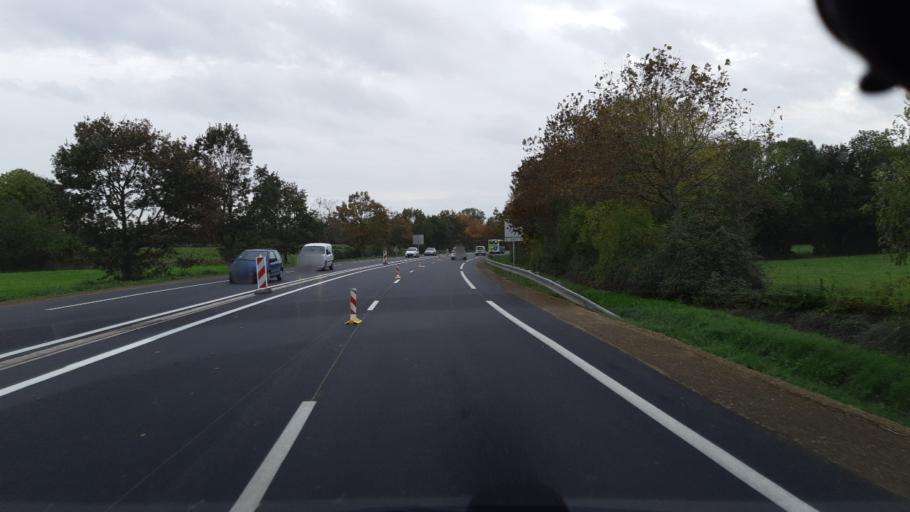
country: FR
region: Lower Normandy
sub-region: Departement de la Manche
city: Brehal
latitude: 48.8955
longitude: -1.5027
